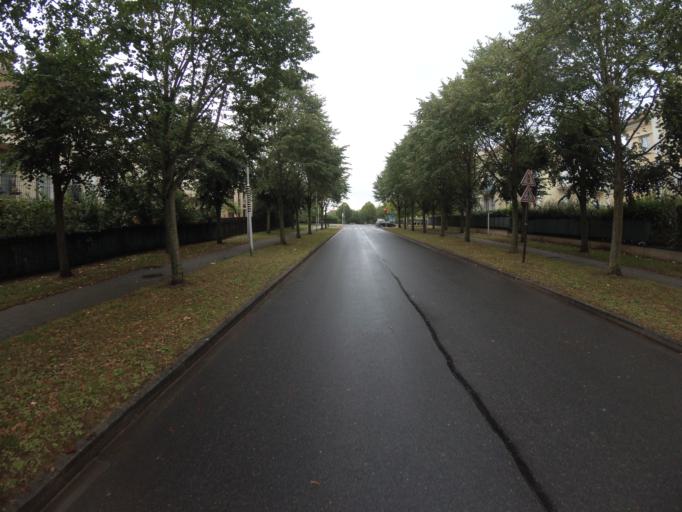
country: FR
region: Ile-de-France
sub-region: Departement de Seine-et-Marne
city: Conches-sur-Gondoire
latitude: 48.8406
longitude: 2.7268
